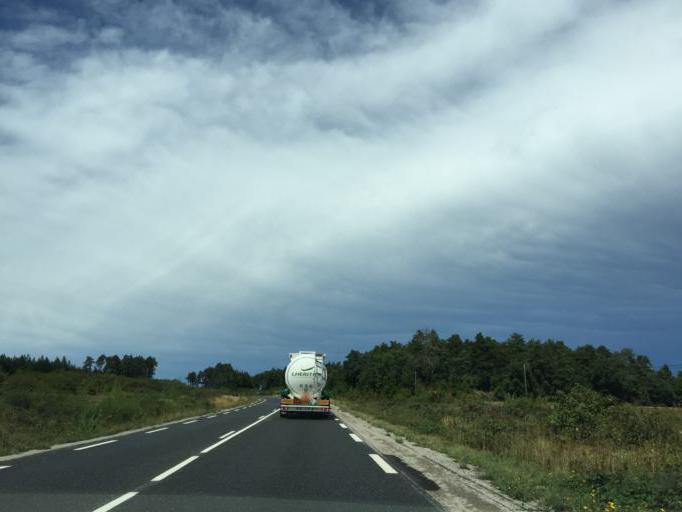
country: FR
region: Midi-Pyrenees
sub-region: Departement de l'Aveyron
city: Millau
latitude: 44.1901
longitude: 3.0252
